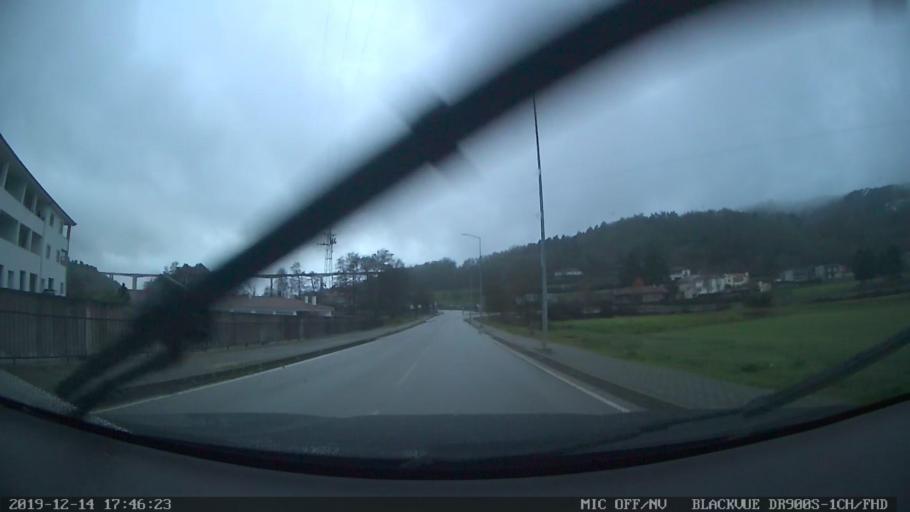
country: PT
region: Vila Real
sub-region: Vila Pouca de Aguiar
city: Vila Pouca de Aguiar
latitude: 41.4906
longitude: -7.6468
